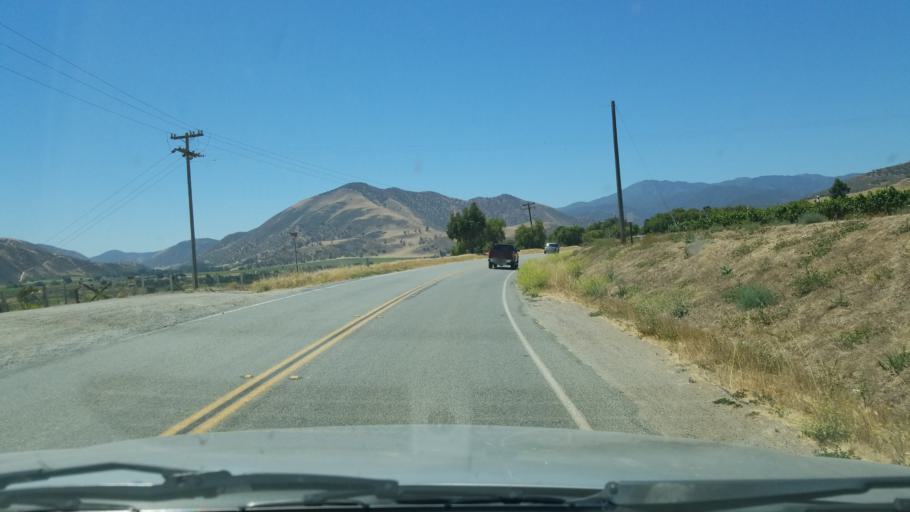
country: US
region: California
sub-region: Monterey County
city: Greenfield
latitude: 36.3046
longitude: -121.3117
